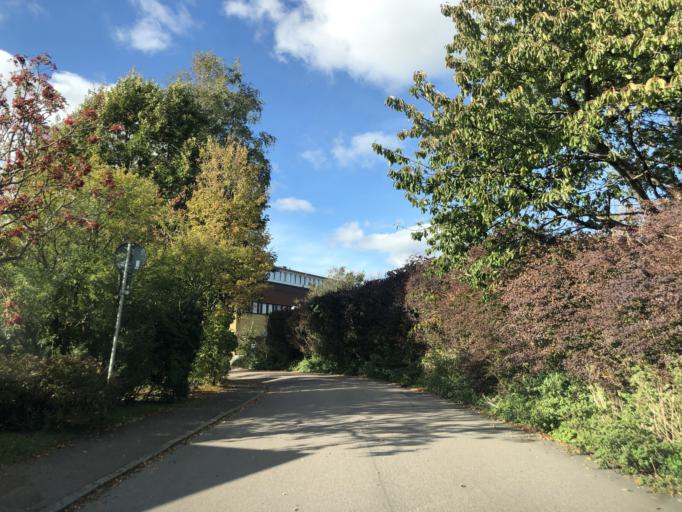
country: SE
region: Vaestra Goetaland
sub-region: Goteborg
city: Majorna
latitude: 57.6329
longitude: 11.9383
